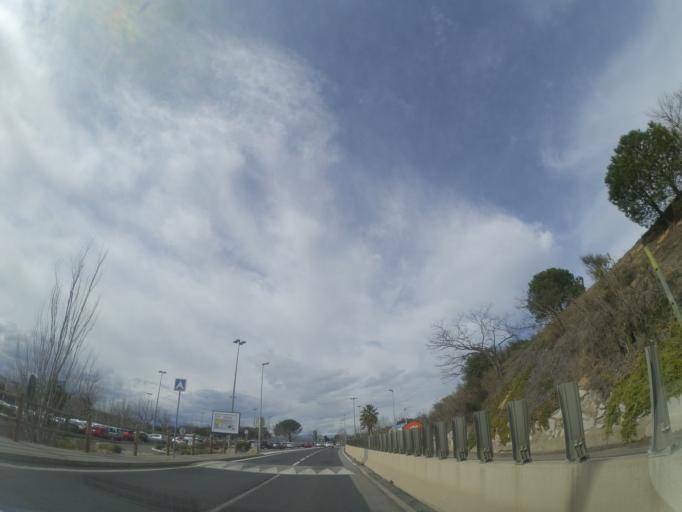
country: FR
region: Languedoc-Roussillon
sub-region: Departement des Pyrenees-Orientales
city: Perpignan
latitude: 42.6704
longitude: 2.8836
